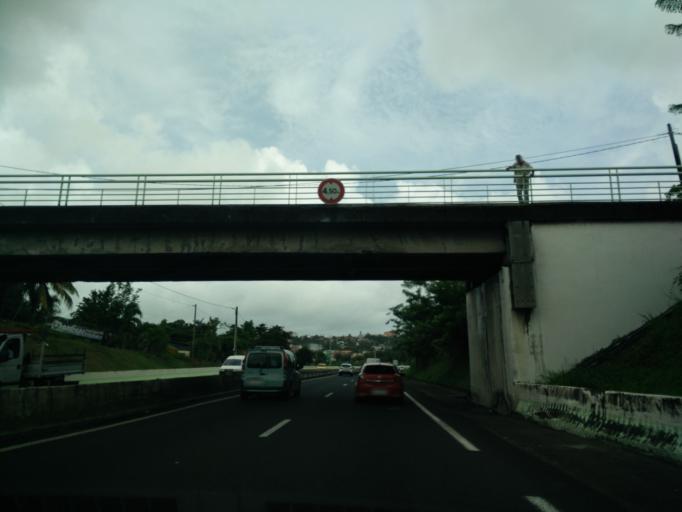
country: MQ
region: Martinique
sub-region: Martinique
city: Ducos
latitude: 14.5862
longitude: -60.9809
